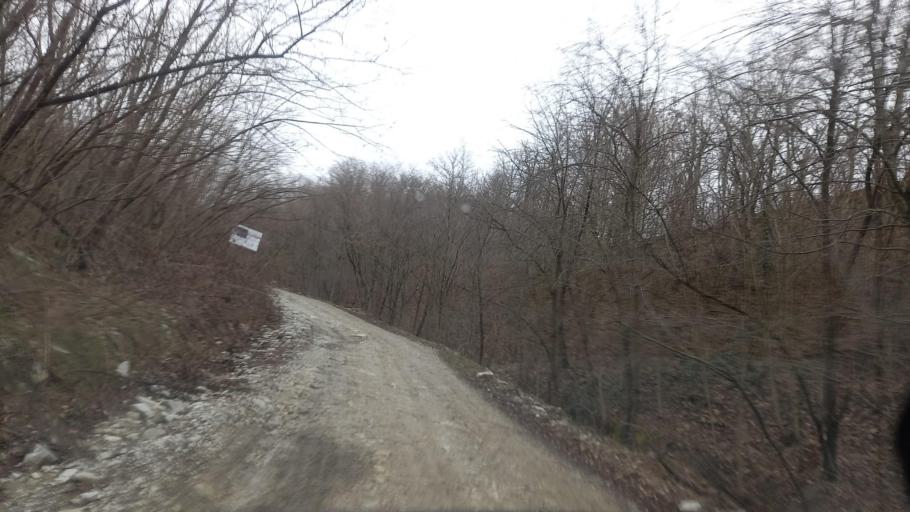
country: RU
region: Krasnodarskiy
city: Divnomorskoye
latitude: 44.5468
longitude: 38.2367
